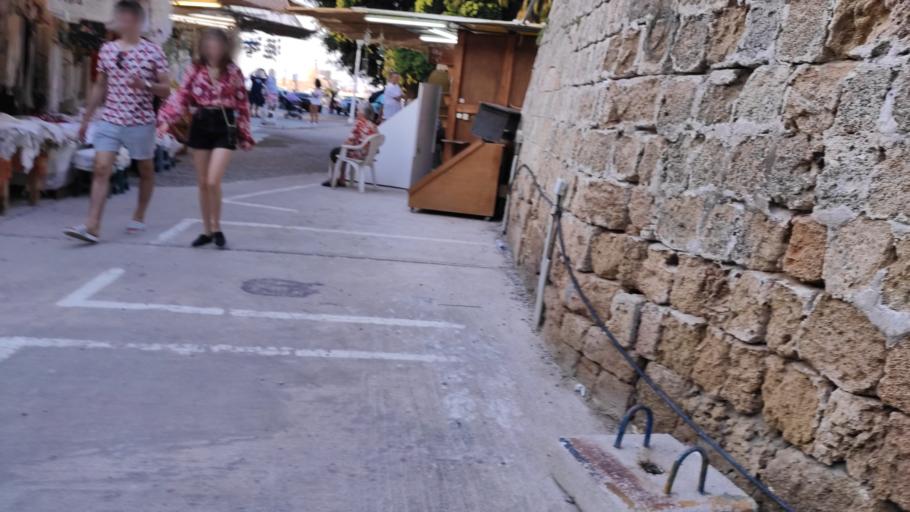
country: GR
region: South Aegean
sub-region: Nomos Dodekanisou
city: Rodos
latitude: 36.4468
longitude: 28.2261
